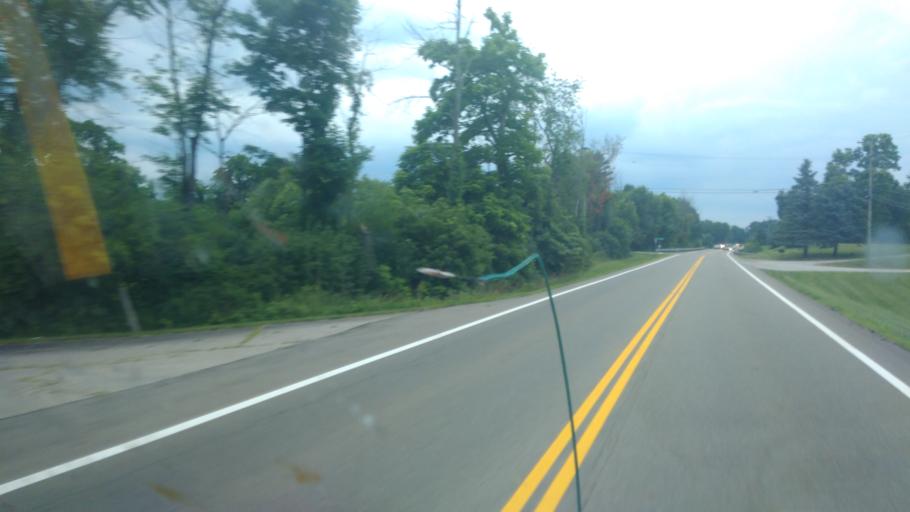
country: US
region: Ohio
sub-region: Licking County
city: Granville South
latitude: 40.0358
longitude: -82.5229
